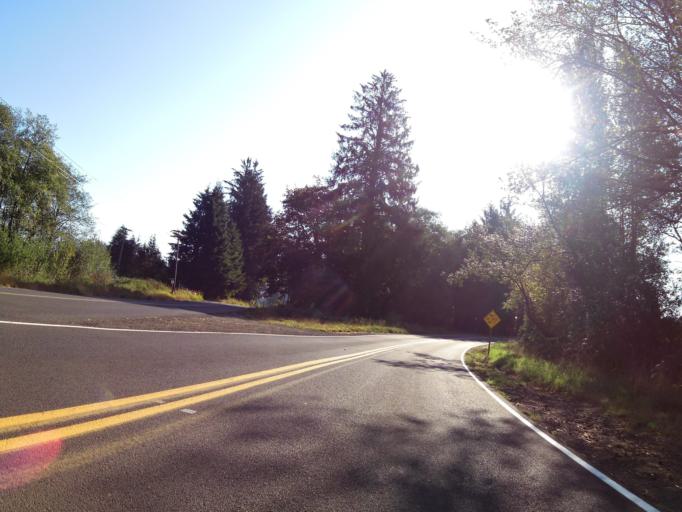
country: US
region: Oregon
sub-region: Tillamook County
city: Tillamook
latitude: 45.4013
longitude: -123.7945
